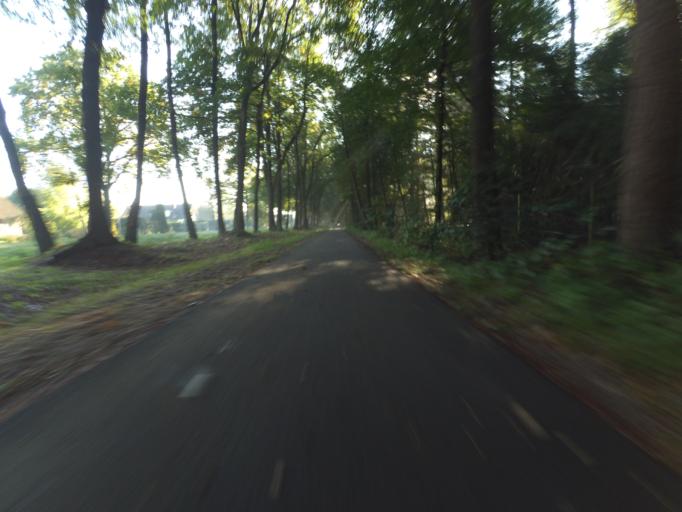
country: NL
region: Gelderland
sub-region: Gemeente Apeldoorn
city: Apeldoorn
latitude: 52.2447
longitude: 5.9488
